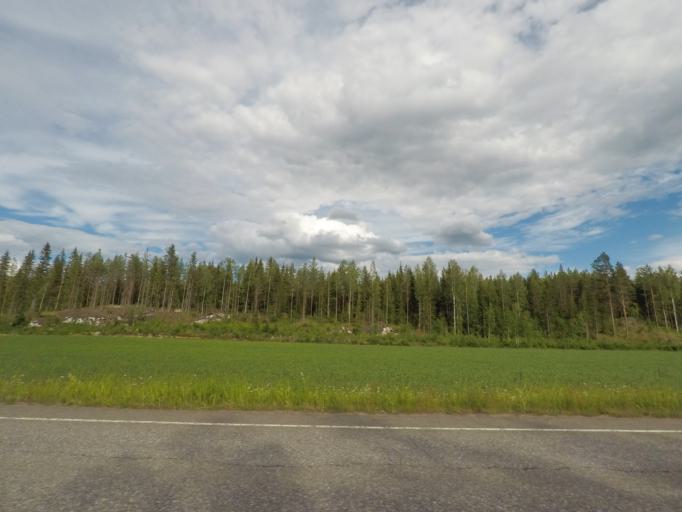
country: FI
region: Paijanne Tavastia
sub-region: Lahti
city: Hollola
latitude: 60.8373
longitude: 25.4929
